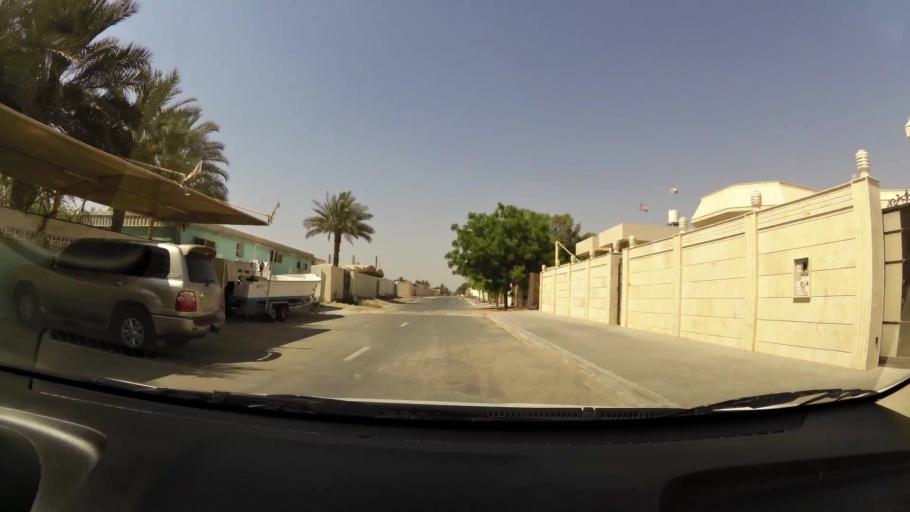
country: AE
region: Ajman
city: Ajman
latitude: 25.4057
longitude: 55.4761
